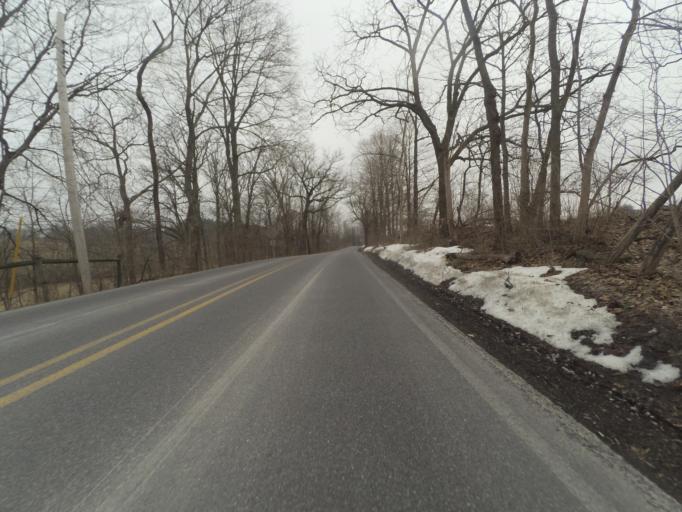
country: US
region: Pennsylvania
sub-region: Centre County
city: Boalsburg
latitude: 40.8077
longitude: -77.7442
